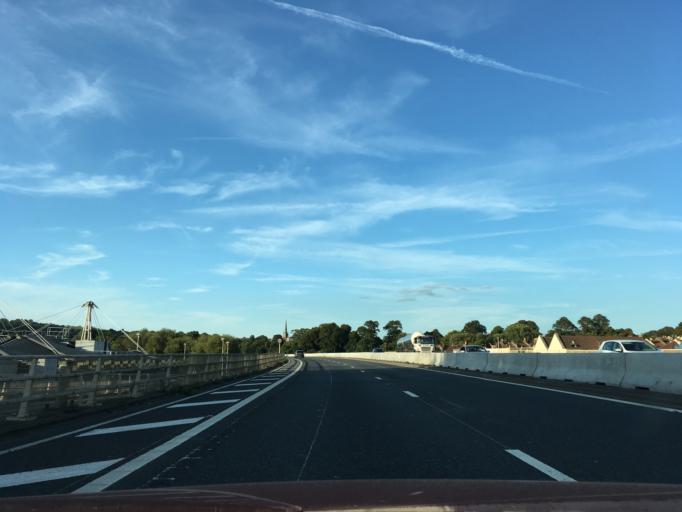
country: GB
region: England
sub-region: Bristol
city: Bristol
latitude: 51.4723
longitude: -2.5627
